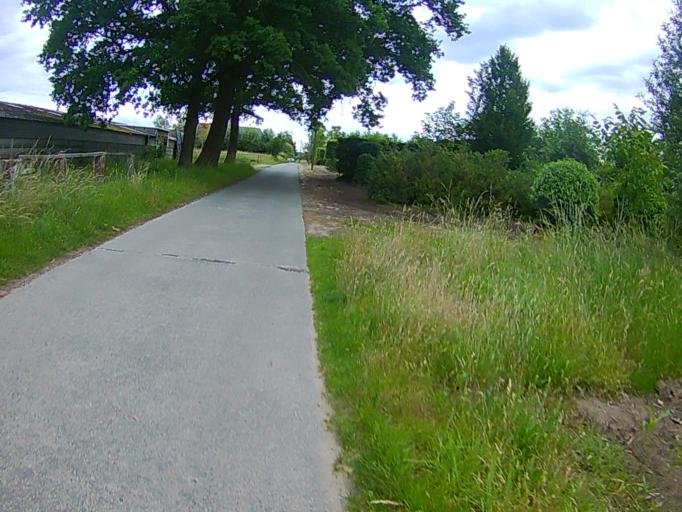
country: BE
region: Flanders
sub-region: Provincie Antwerpen
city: Putte
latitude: 51.0365
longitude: 4.6523
